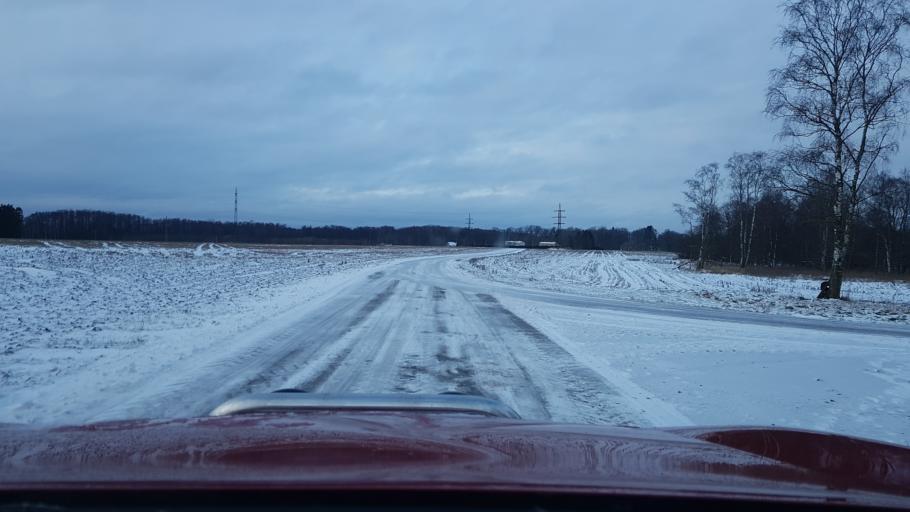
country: EE
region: Harju
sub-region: Maardu linn
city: Maardu
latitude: 59.4210
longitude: 25.0243
